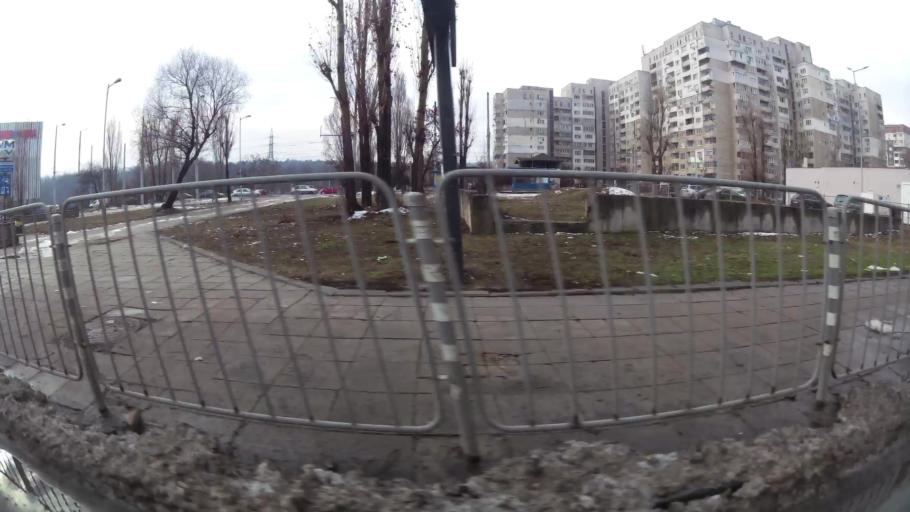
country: BG
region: Sofia-Capital
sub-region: Stolichna Obshtina
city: Sofia
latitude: 42.7115
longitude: 23.2697
